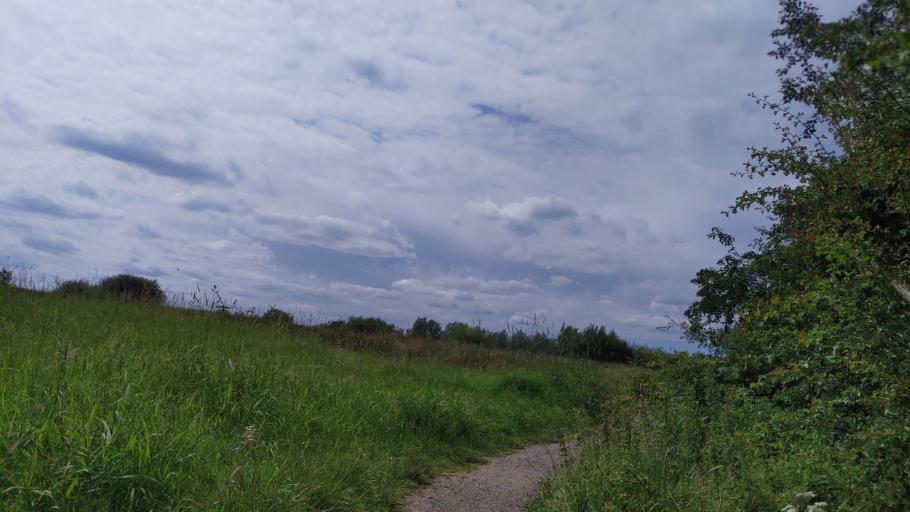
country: GB
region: England
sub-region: Lancashire
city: Coppull
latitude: 53.6354
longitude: -2.6440
